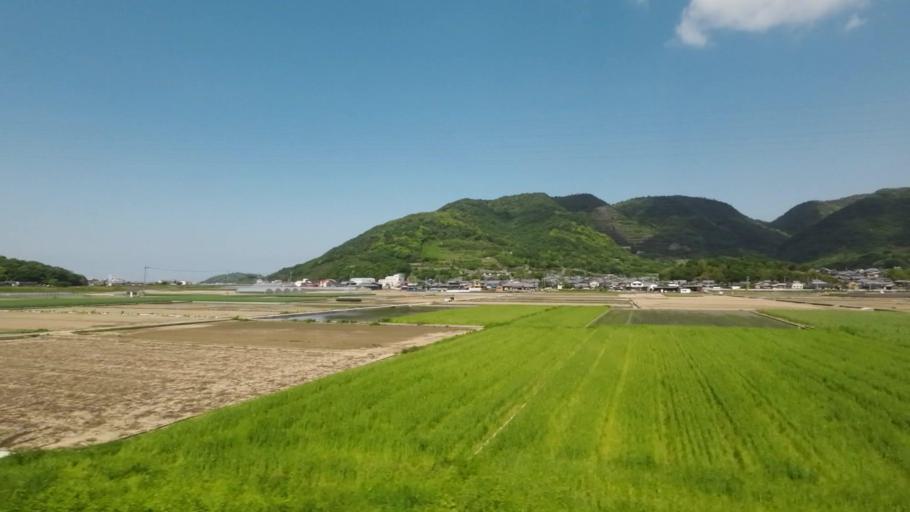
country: JP
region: Kagawa
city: Kan'onjicho
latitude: 34.1411
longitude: 133.6853
